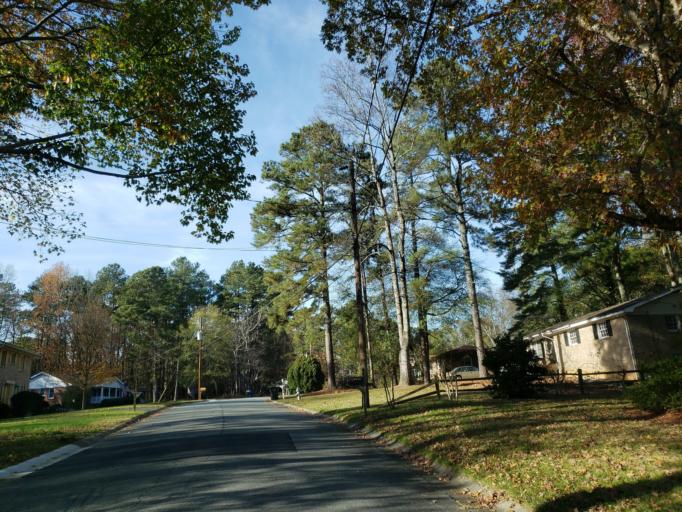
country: US
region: Georgia
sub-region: Cobb County
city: Kennesaw
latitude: 34.0232
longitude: -84.6064
